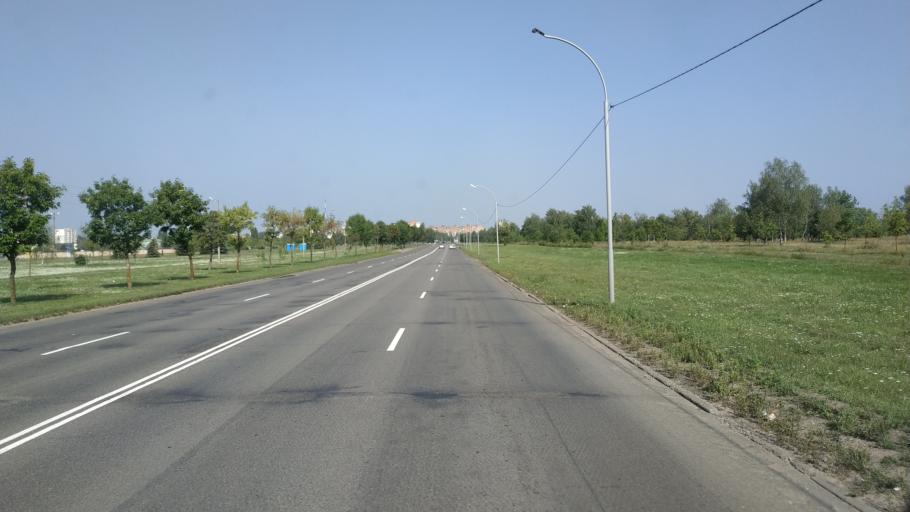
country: BY
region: Mogilev
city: Buynichy
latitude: 53.8606
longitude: 30.3243
